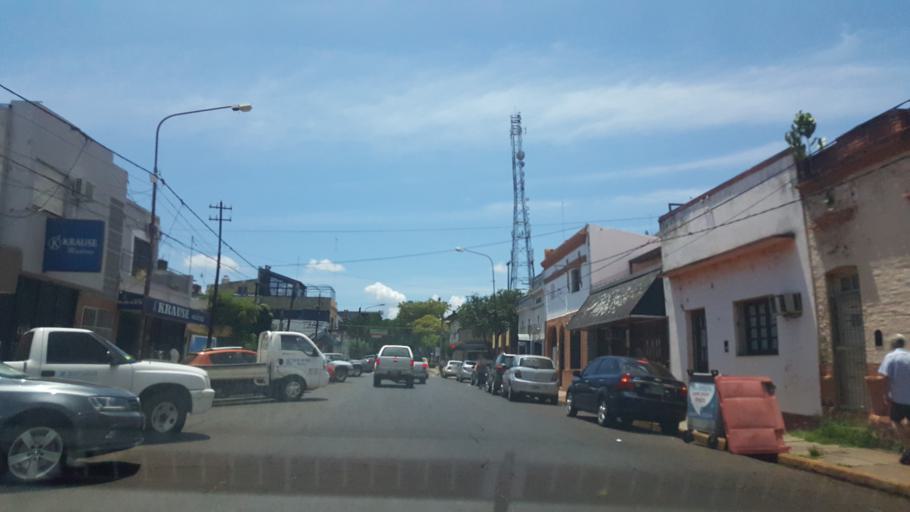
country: AR
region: Misiones
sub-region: Departamento de Capital
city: Posadas
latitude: -27.3637
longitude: -55.8971
